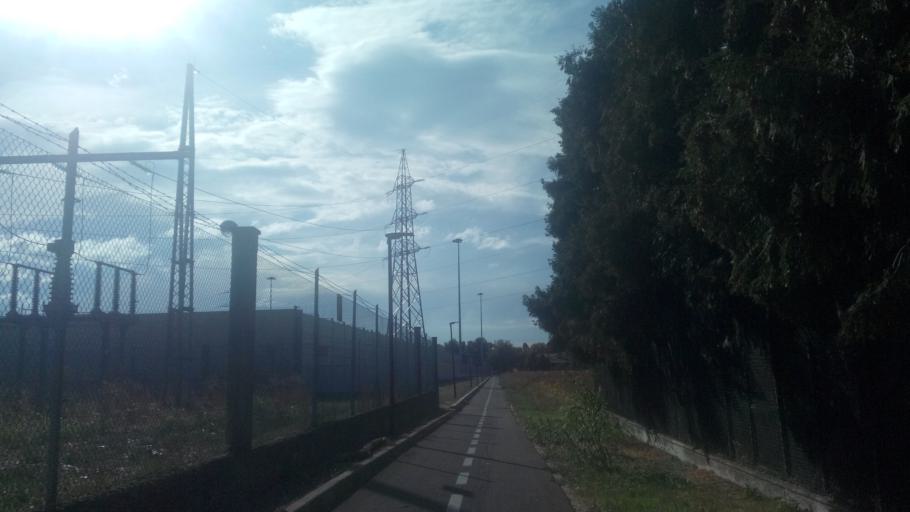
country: IT
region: Emilia-Romagna
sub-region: Provincia di Bologna
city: Bologna
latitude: 44.5230
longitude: 11.3585
